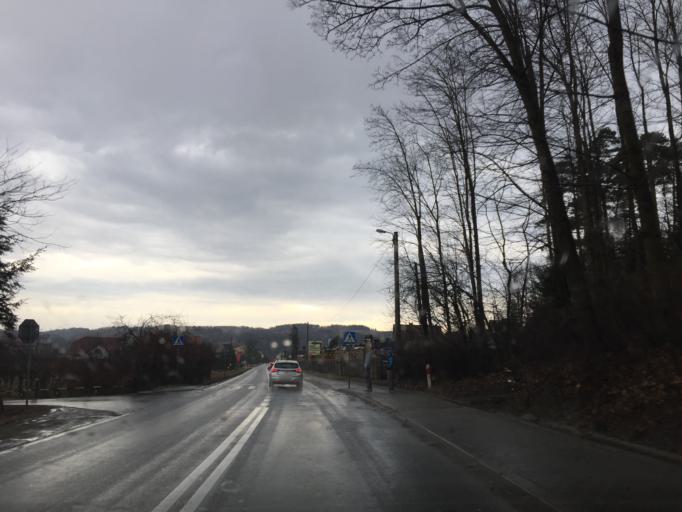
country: PL
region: Lesser Poland Voivodeship
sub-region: Powiat wadowicki
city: Izdebnik
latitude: 49.8685
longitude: 19.7937
